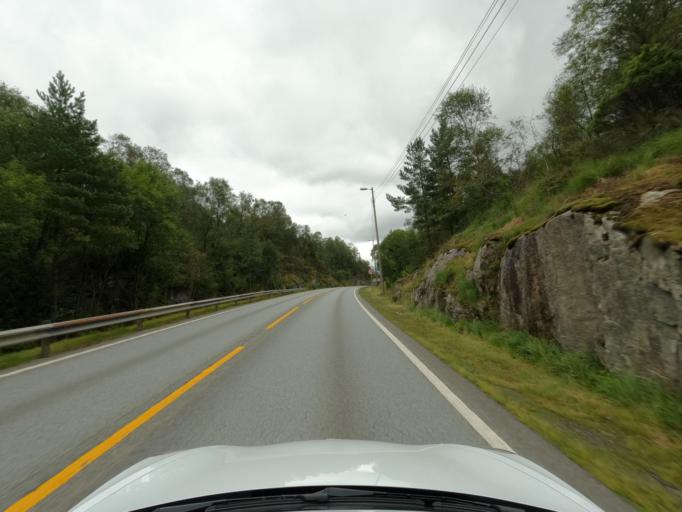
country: NO
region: Hordaland
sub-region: Bergen
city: Indre Arna
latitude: 60.4042
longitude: 5.4694
